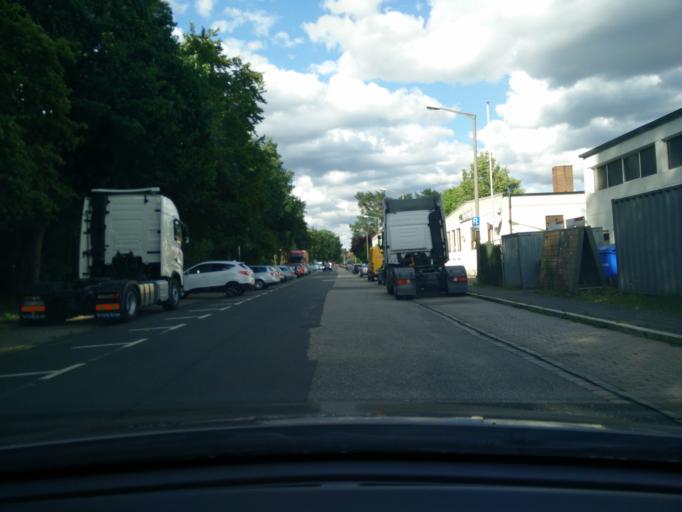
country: DE
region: Bavaria
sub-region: Regierungsbezirk Mittelfranken
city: Wendelstein
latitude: 49.4091
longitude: 11.1628
